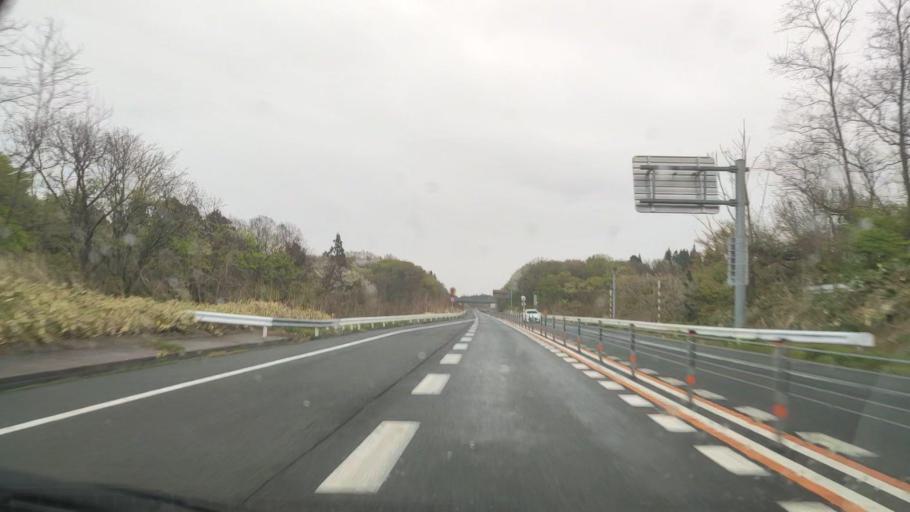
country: JP
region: Akita
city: Noshiromachi
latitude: 40.1502
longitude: 140.0212
